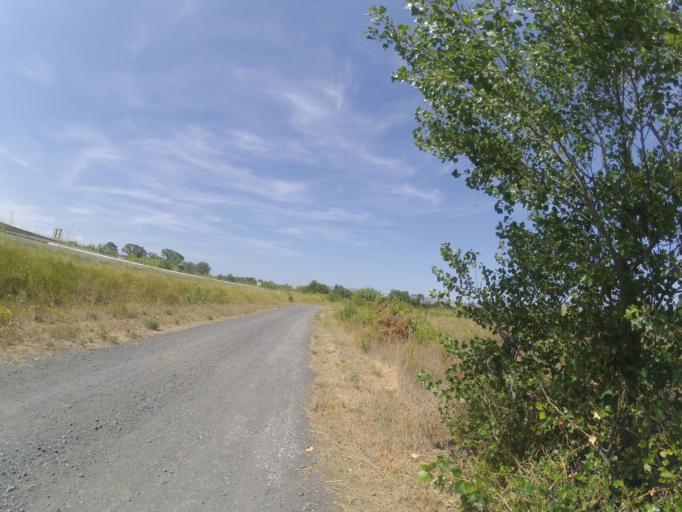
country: FR
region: Languedoc-Roussillon
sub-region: Departement des Pyrenees-Orientales
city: Peyrestortes
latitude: 42.7570
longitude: 2.8576
